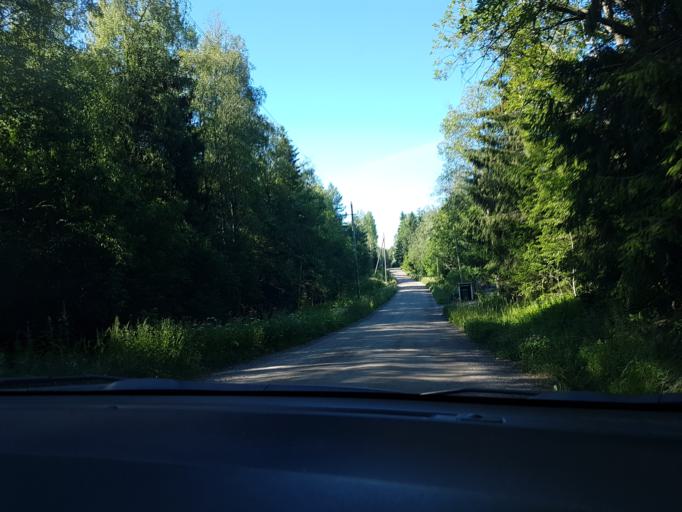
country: FI
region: Uusimaa
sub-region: Helsinki
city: Sibbo
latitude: 60.2821
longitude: 25.2384
